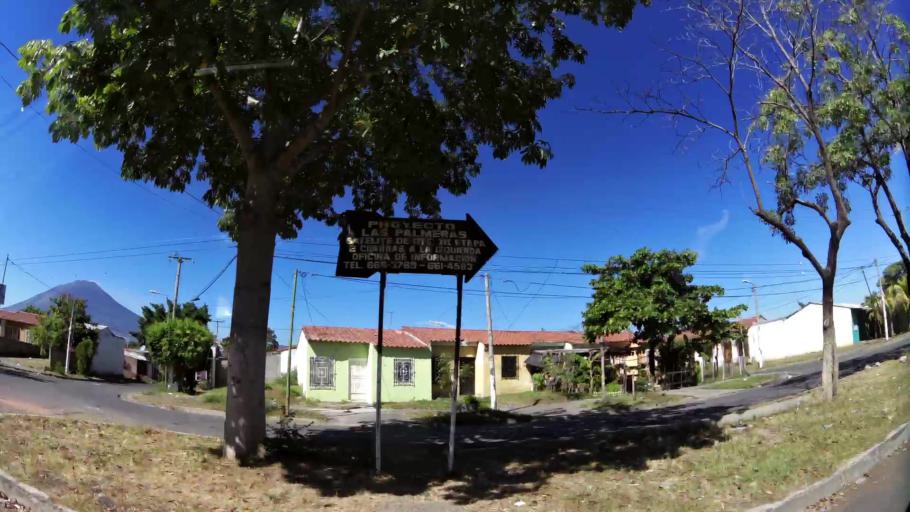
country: SV
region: San Miguel
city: San Miguel
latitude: 13.4927
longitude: -88.1650
